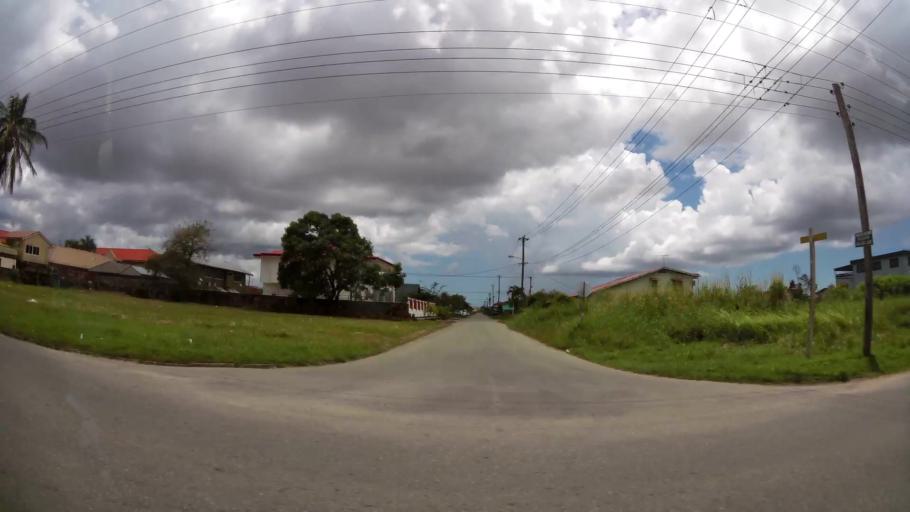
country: SR
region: Paramaribo
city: Paramaribo
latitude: 5.8562
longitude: -55.1357
